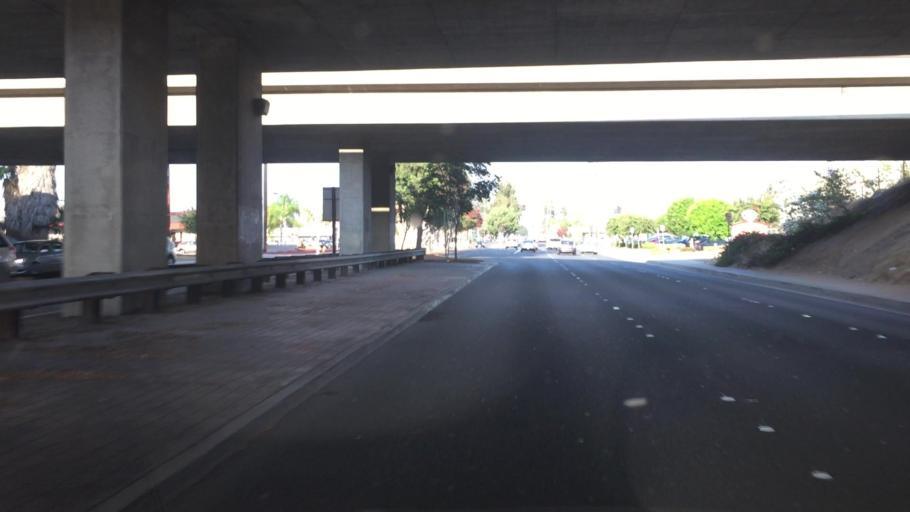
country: US
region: California
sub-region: San Diego County
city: El Cajon
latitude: 32.8077
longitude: -116.9621
